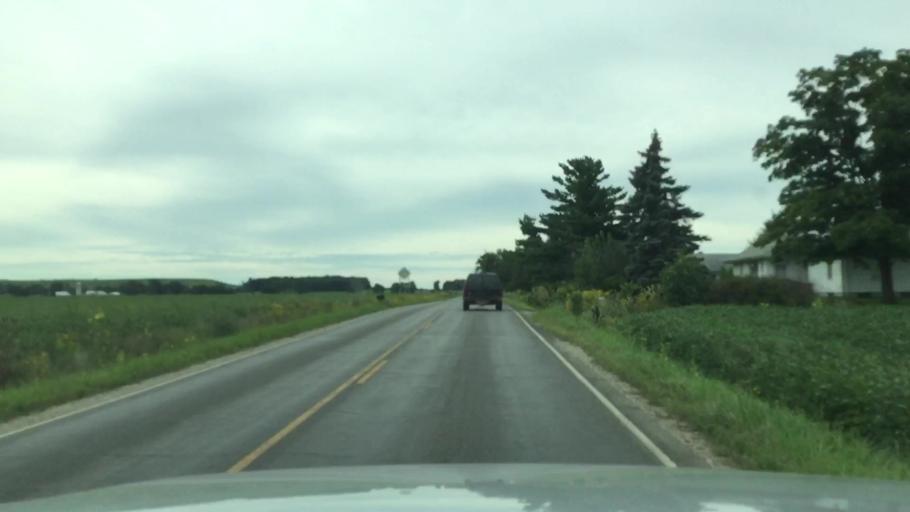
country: US
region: Michigan
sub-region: Shiawassee County
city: Durand
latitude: 42.9983
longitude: -83.9868
